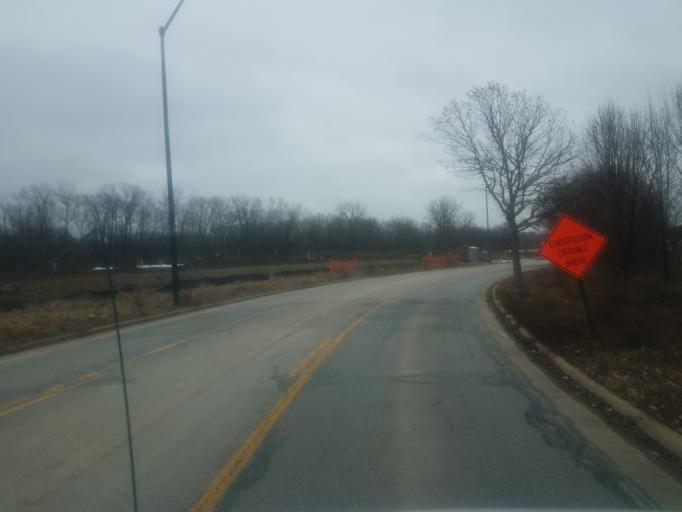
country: US
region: Ohio
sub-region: Franklin County
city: Westerville
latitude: 40.1203
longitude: -82.9409
